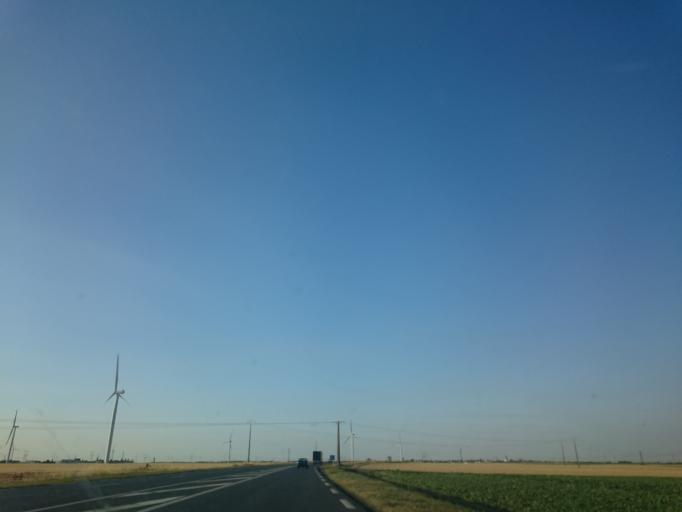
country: FR
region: Centre
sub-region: Departement d'Eure-et-Loir
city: Toury
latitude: 48.1557
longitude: 1.9094
